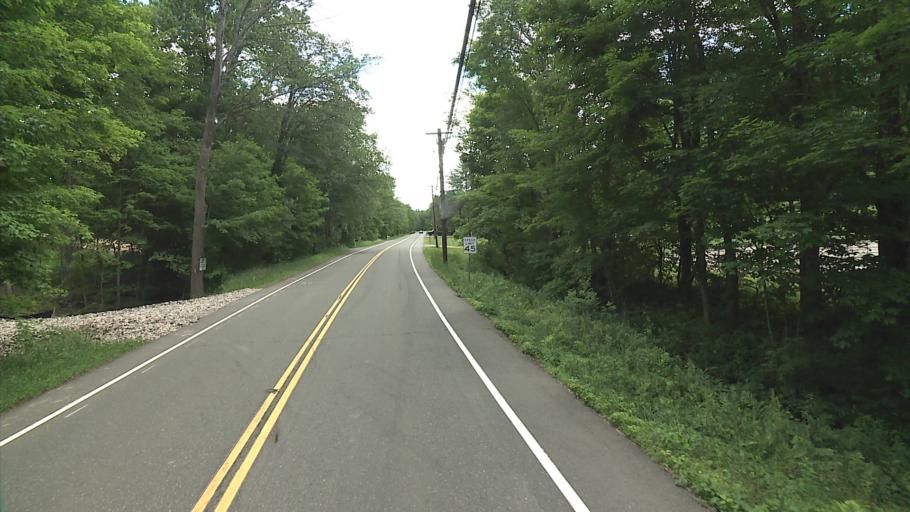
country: US
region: Connecticut
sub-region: Litchfield County
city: Bethlehem Village
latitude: 41.6682
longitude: -73.1648
